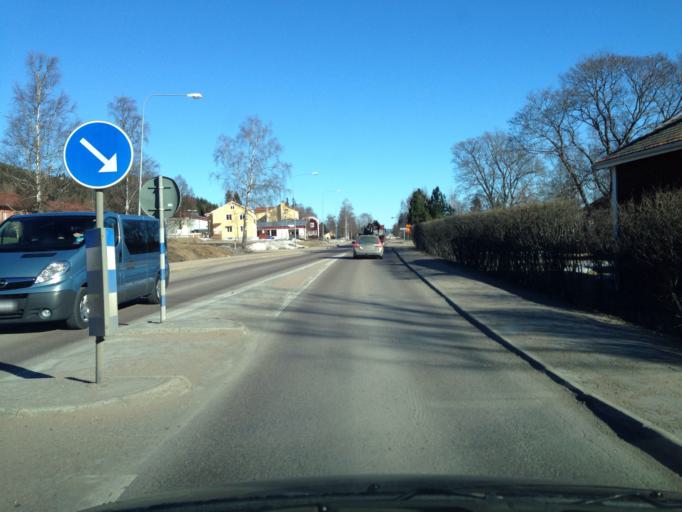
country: SE
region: Gaevleborg
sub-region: Ljusdals Kommun
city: Jaervsoe
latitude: 61.7069
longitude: 16.1632
